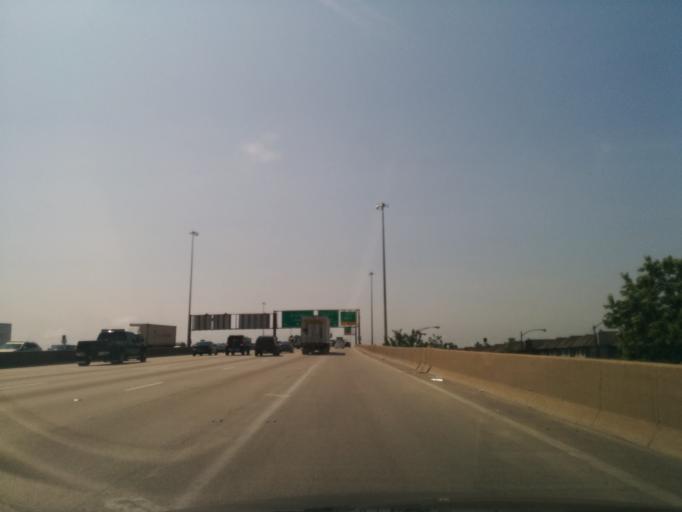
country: US
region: Illinois
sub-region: Cook County
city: Chicago
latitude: 41.8640
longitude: -87.6449
